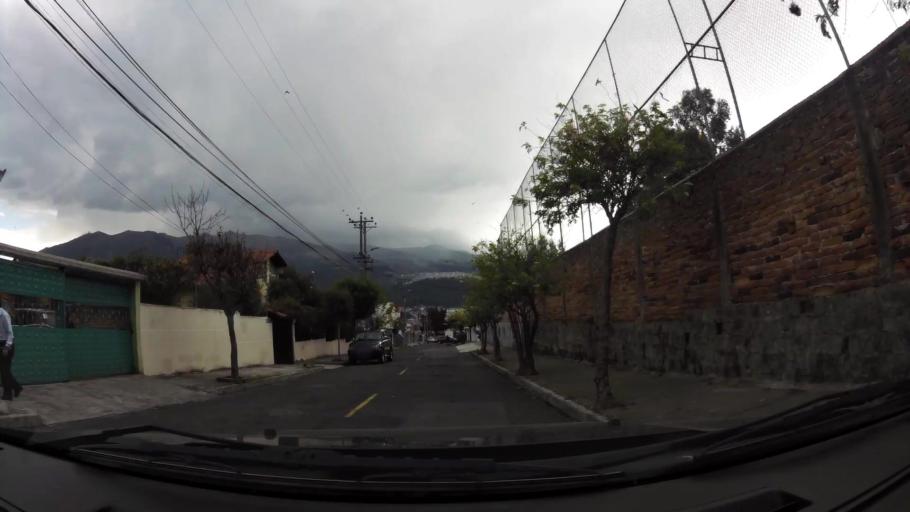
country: EC
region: Pichincha
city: Quito
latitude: -0.1317
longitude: -78.4855
